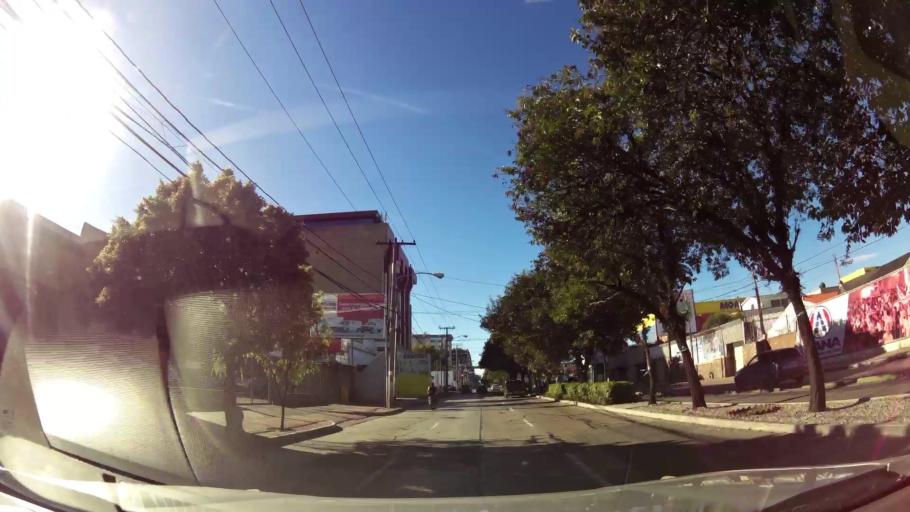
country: GT
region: Guatemala
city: Guatemala City
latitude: 14.6116
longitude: -90.5186
